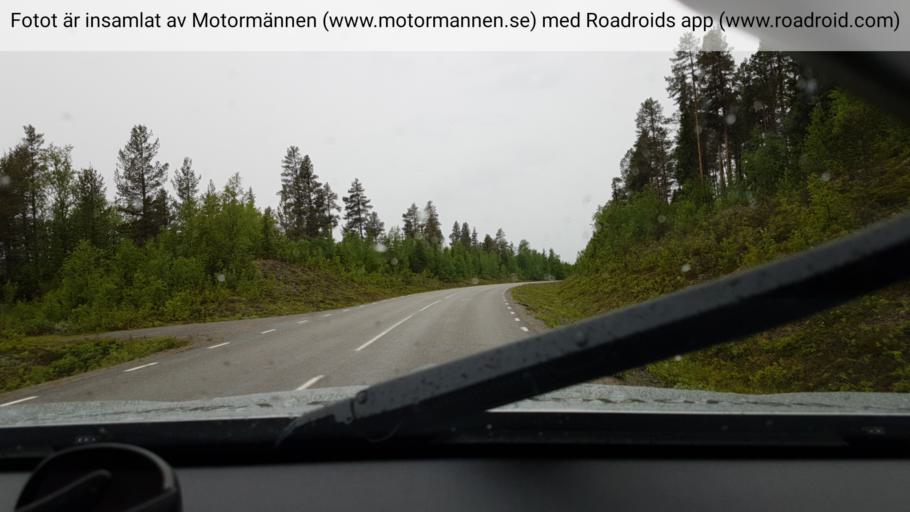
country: SE
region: Vaesterbotten
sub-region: Storumans Kommun
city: Fristad
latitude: 65.8502
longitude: 16.5580
